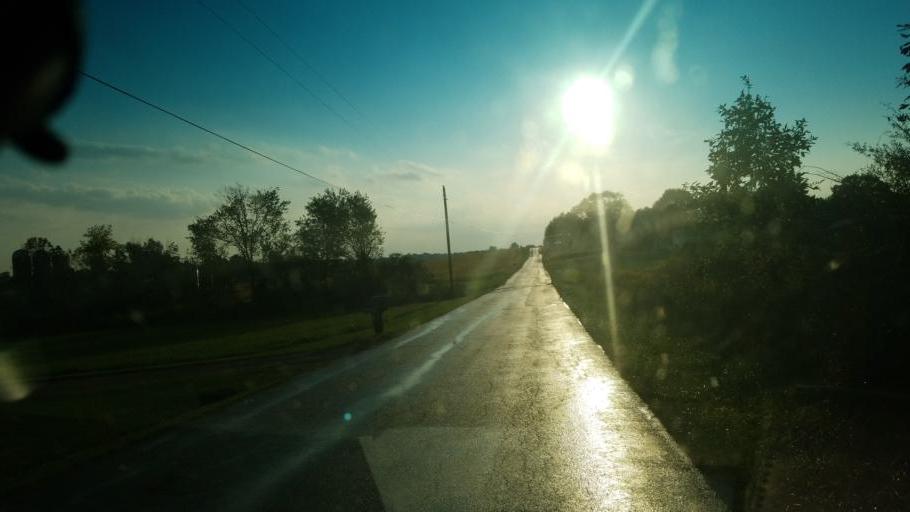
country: US
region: Ohio
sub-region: Knox County
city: Fredericktown
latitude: 40.5333
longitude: -82.5396
